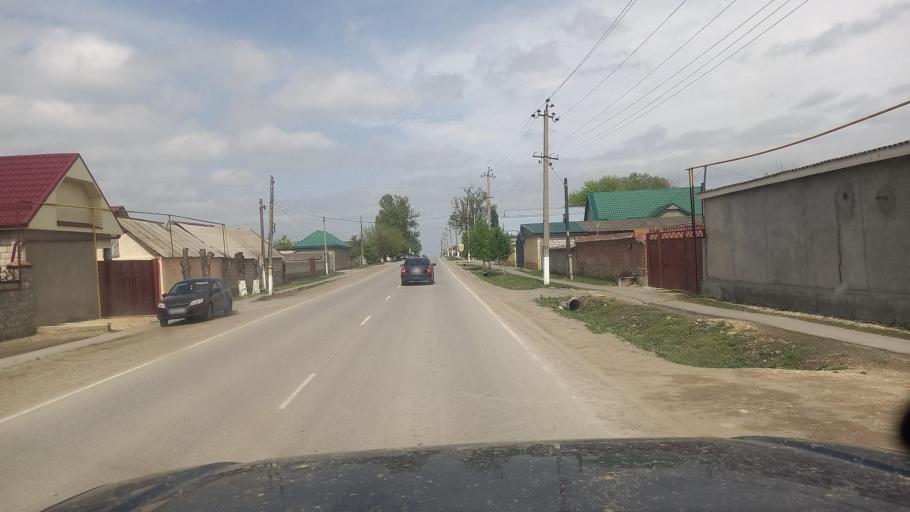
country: RU
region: Kabardino-Balkariya
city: Sarmakovo
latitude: 43.7341
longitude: 43.1757
